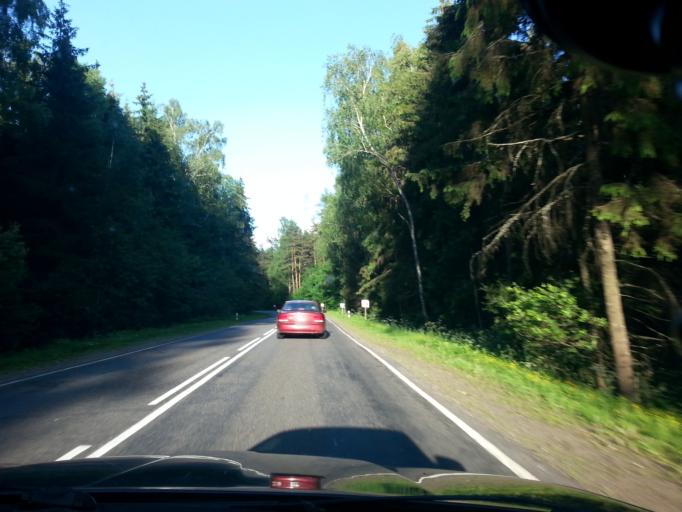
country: BY
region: Minsk
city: Svir
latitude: 54.9221
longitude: 26.5130
